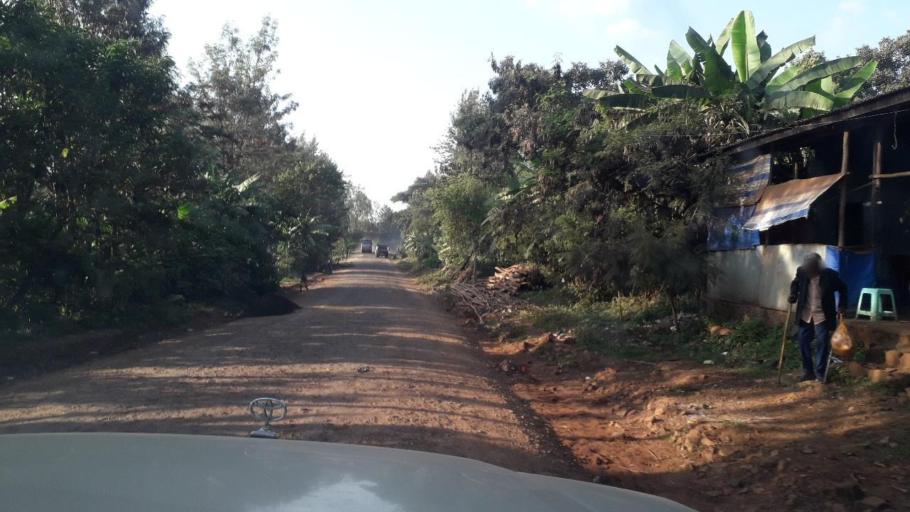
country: ET
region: Oromiya
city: Jima
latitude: 7.5811
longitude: 36.8587
